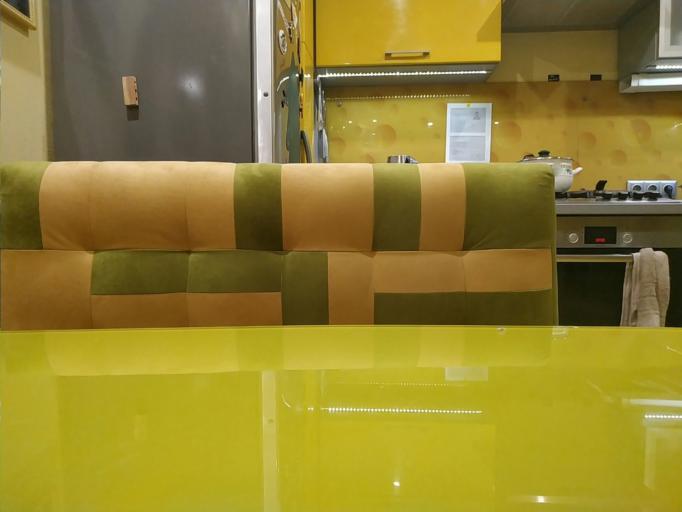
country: RU
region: Murmansk
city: Alakurtti
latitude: 66.1550
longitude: 30.3108
